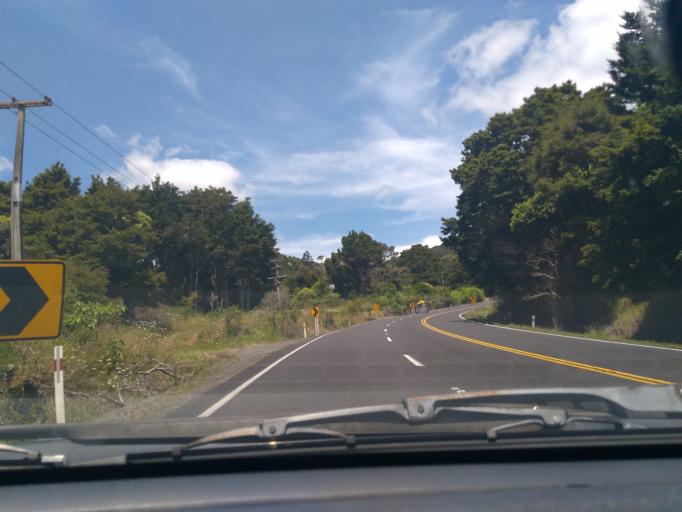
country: NZ
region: Northland
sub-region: Far North District
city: Kerikeri
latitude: -35.1182
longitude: 173.8198
